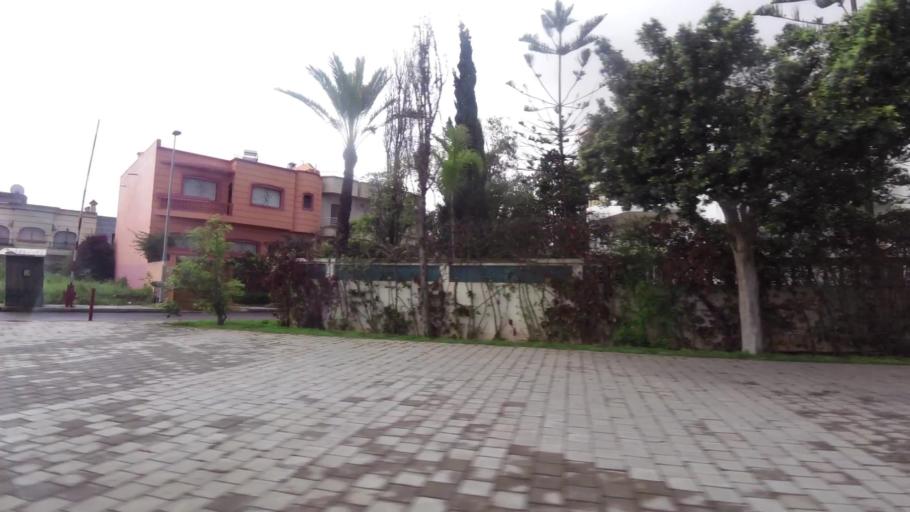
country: MA
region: Grand Casablanca
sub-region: Casablanca
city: Casablanca
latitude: 33.5475
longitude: -7.6576
